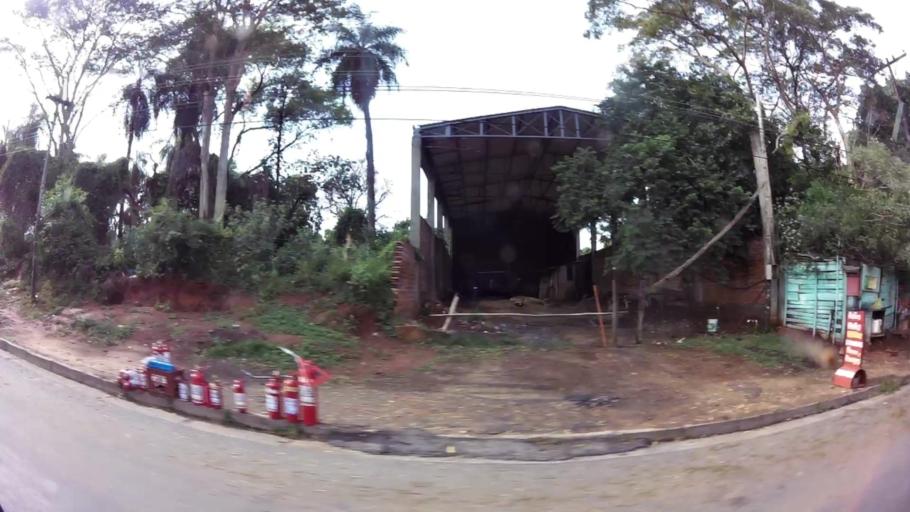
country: PY
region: Central
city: Limpio
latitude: -25.1677
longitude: -57.4723
